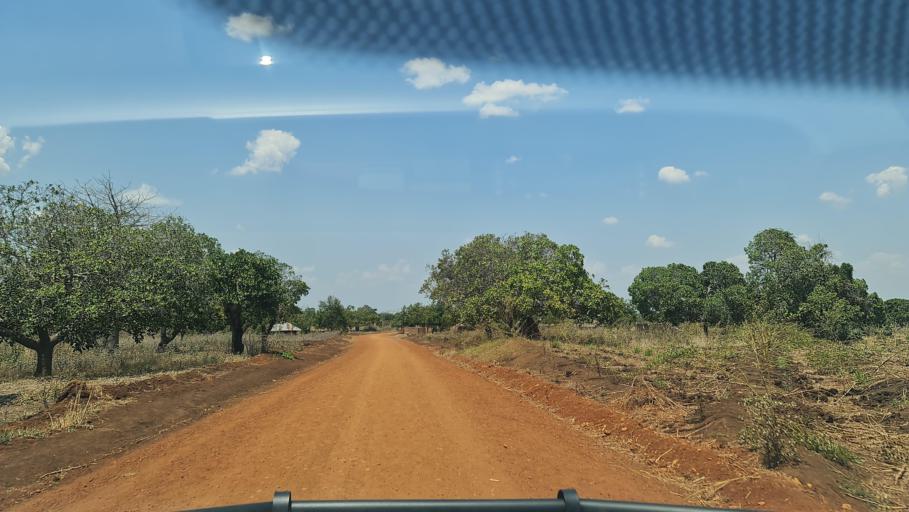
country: MZ
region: Nampula
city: Nacala
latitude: -14.8008
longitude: 40.0706
